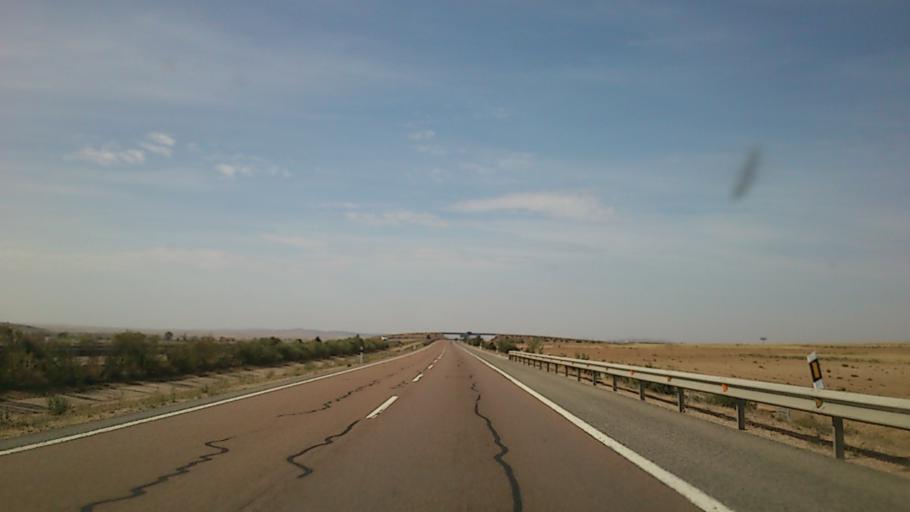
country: ES
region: Aragon
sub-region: Provincia de Teruel
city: Singra
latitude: 40.6829
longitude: -1.3161
